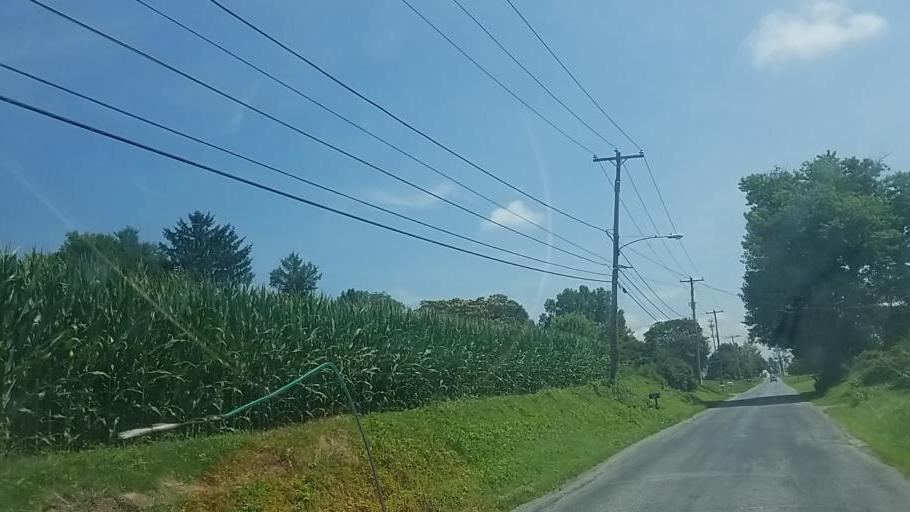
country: US
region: Pennsylvania
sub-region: Chester County
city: Parkesburg
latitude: 39.8910
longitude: -75.9280
